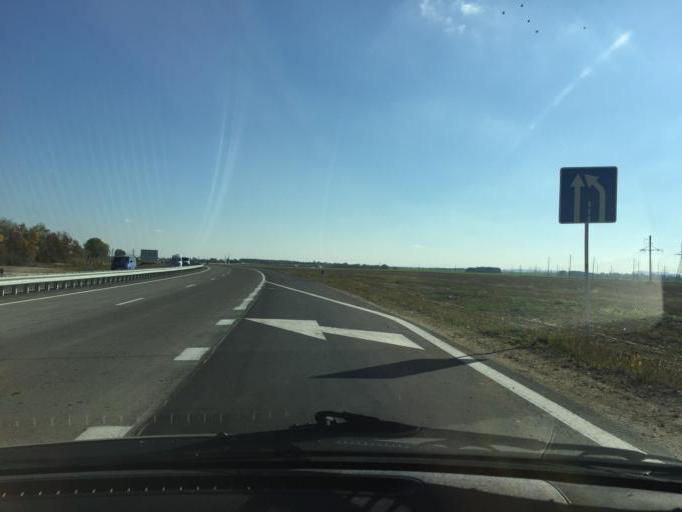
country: BY
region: Minsk
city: Slutsk
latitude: 53.0061
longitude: 27.4891
